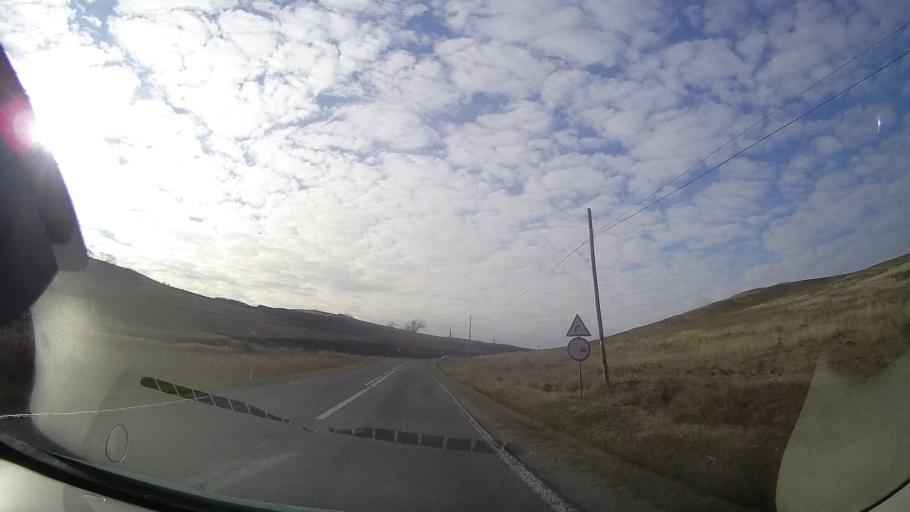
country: RO
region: Cluj
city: Jucu Herghelia
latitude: 46.8111
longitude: 23.8066
